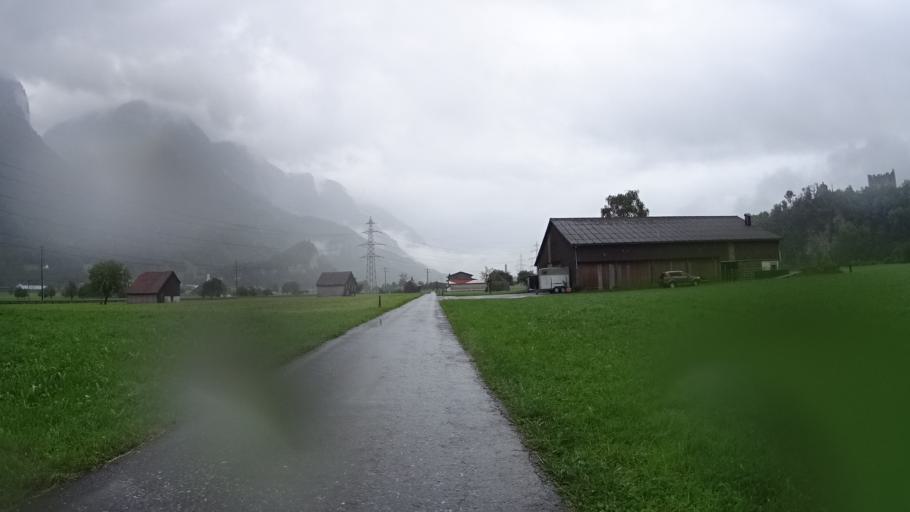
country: CH
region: Saint Gallen
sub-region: Wahlkreis Sarganserland
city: Flums
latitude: 47.1074
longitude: 9.3313
